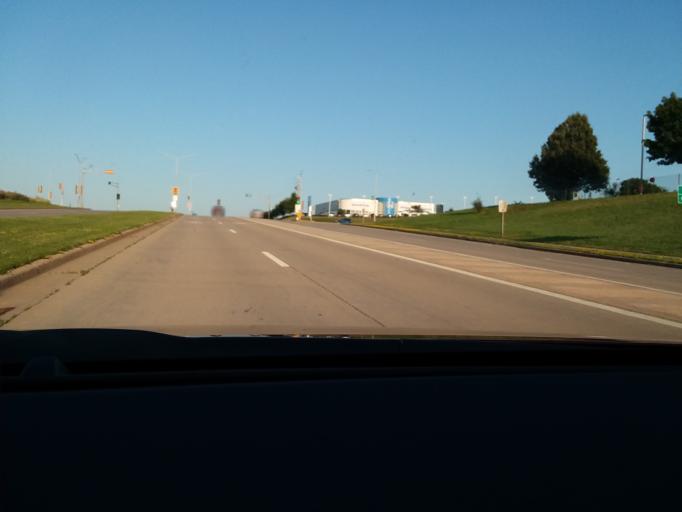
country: US
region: Wisconsin
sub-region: Dane County
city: Sun Prairie
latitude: 43.1450
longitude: -89.2842
